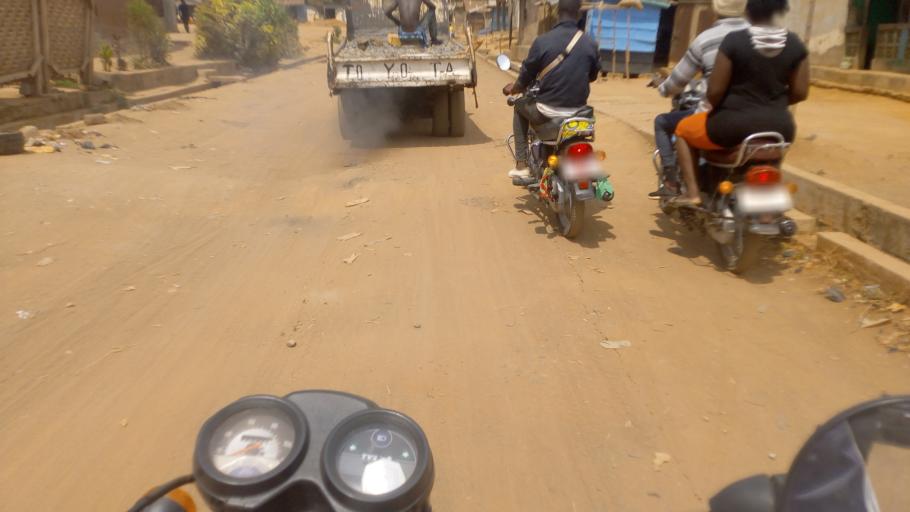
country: SL
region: Western Area
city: Waterloo
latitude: 8.3211
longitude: -13.0687
